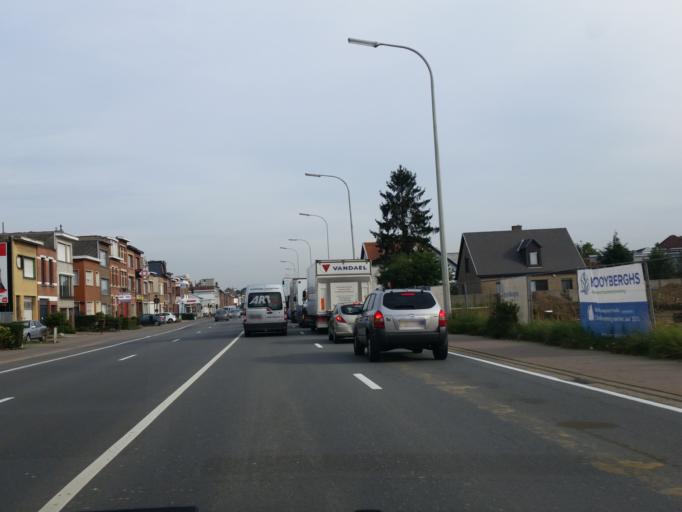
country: BE
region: Flanders
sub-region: Provincie Antwerpen
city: Borsbeek
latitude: 51.2011
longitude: 4.4844
